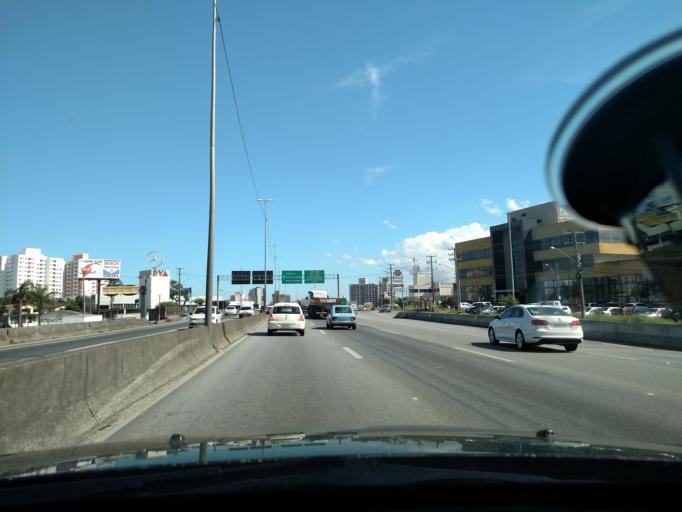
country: BR
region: Santa Catarina
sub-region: Sao Jose
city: Campinas
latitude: -27.5751
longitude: -48.6135
